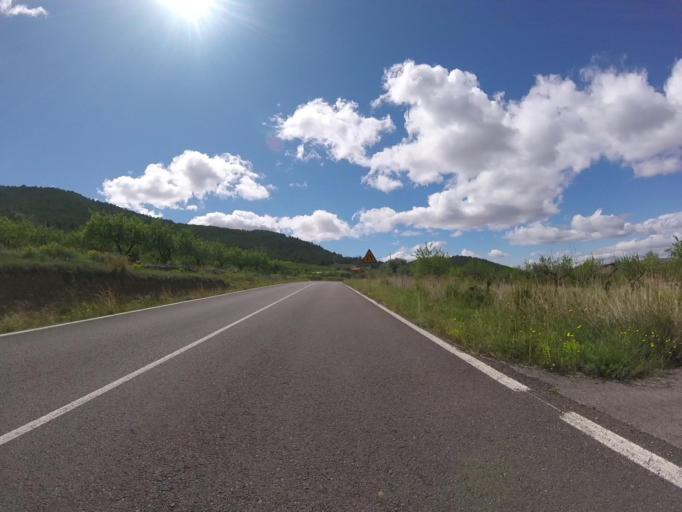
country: ES
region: Valencia
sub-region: Provincia de Castello
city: Culla
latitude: 40.2846
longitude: -0.1127
